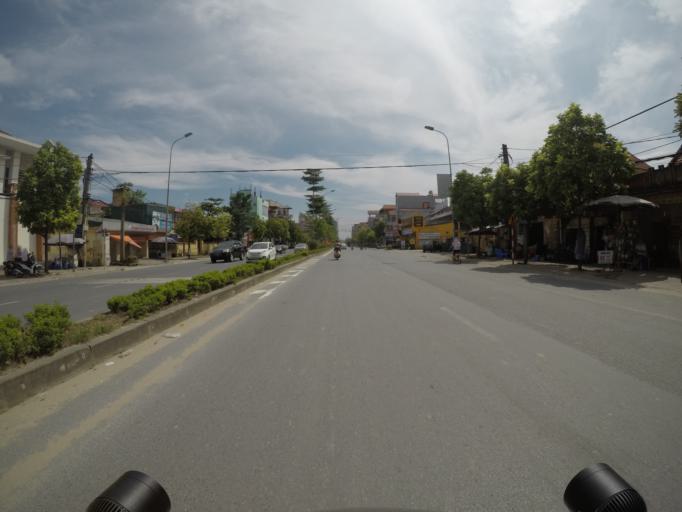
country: VN
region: Ha Noi
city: Troi
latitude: 21.0696
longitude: 105.7083
